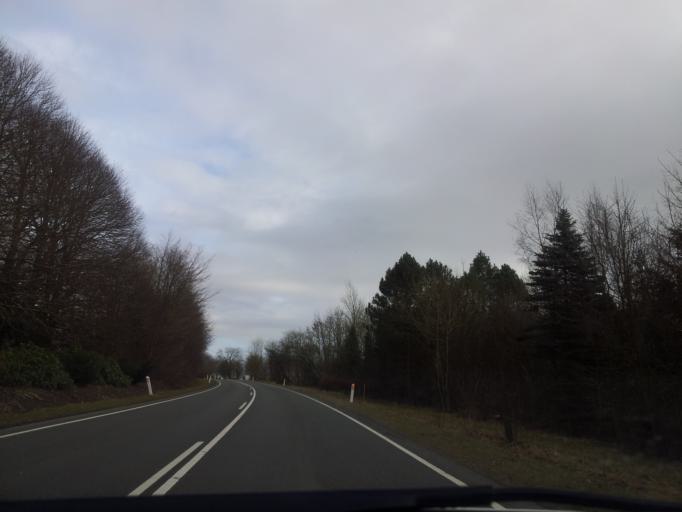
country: DK
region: South Denmark
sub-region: Vejen Kommune
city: Brorup
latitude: 55.4405
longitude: 9.0646
